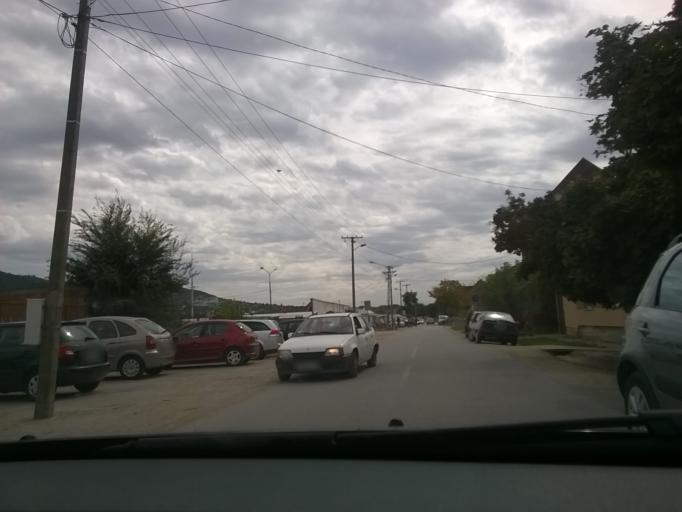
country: RS
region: Autonomna Pokrajina Vojvodina
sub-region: Juznobanatski Okrug
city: Vrsac
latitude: 45.1275
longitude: 21.2976
